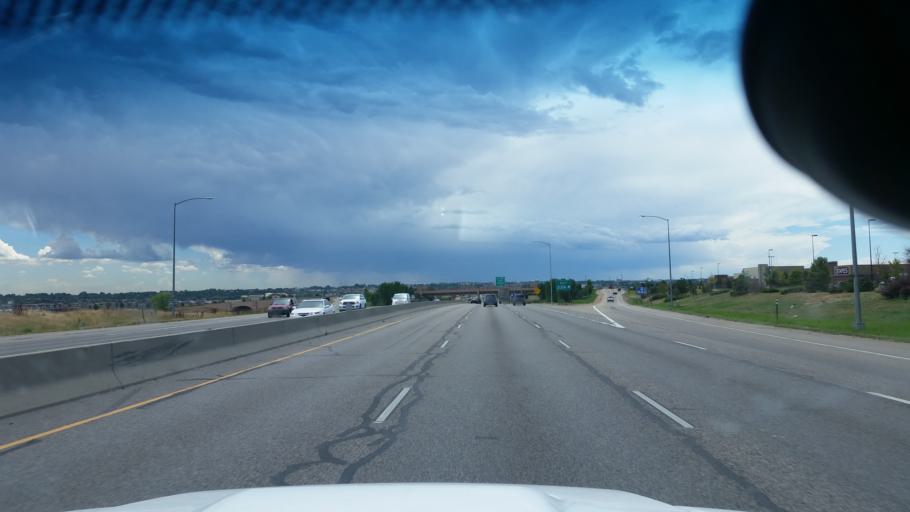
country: US
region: Colorado
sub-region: Adams County
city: Northglenn
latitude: 39.9627
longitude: -104.9882
